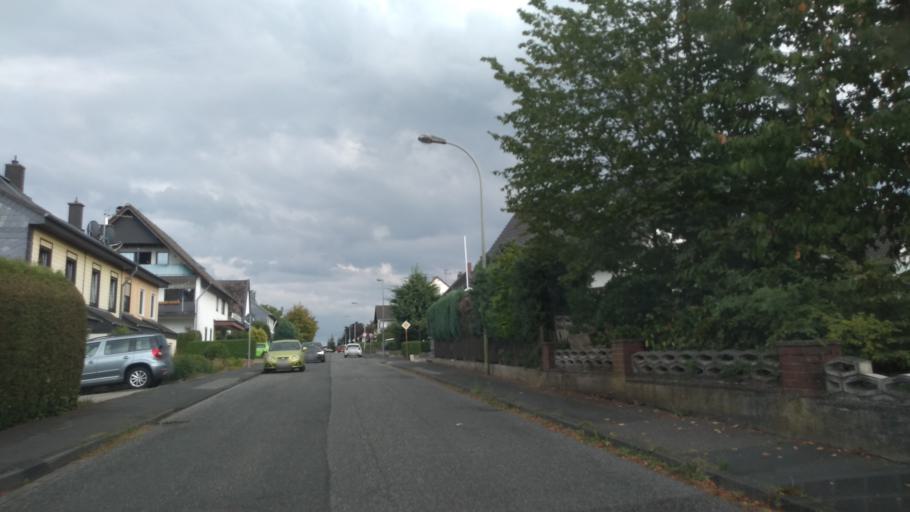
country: DE
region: North Rhine-Westphalia
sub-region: Regierungsbezirk Koln
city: Hennef
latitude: 50.8339
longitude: 7.2807
